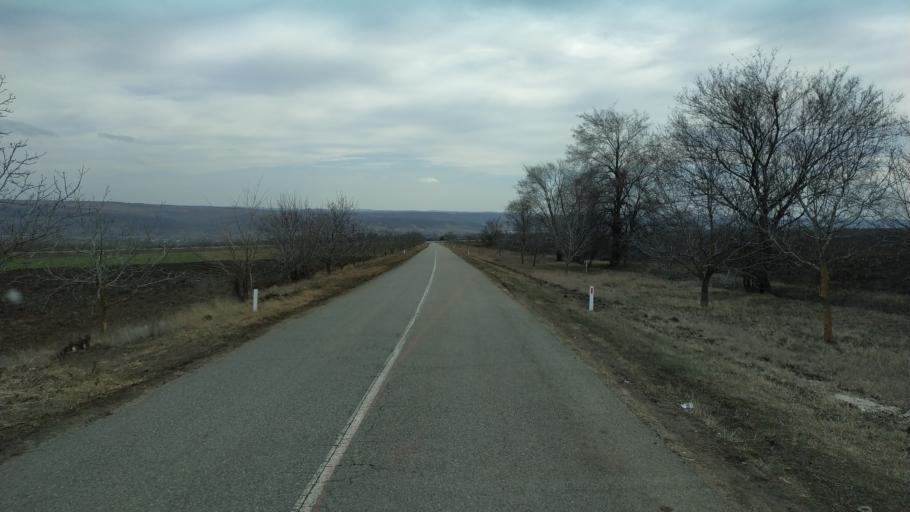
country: MD
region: Nisporeni
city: Nisporeni
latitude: 46.9414
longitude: 28.2441
